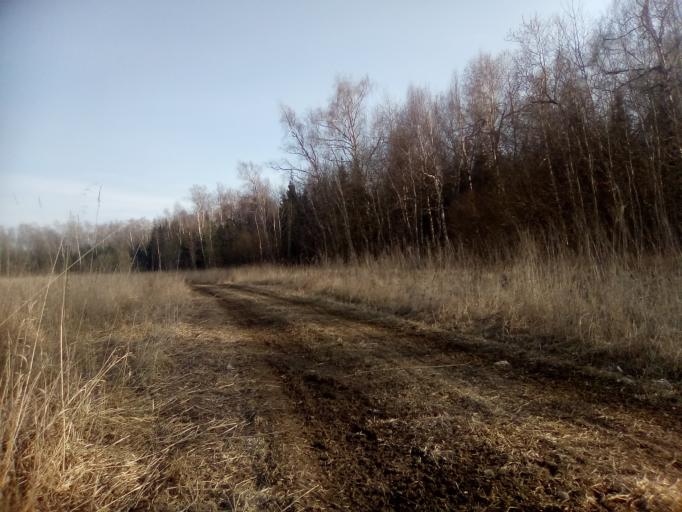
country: RU
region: Moskovskaya
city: Dubrovitsy
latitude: 55.4699
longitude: 37.4184
